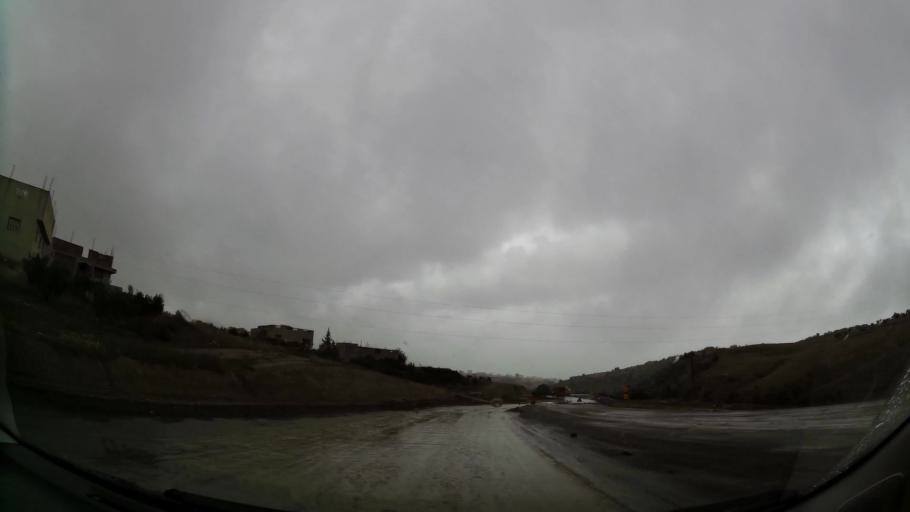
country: MA
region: Oriental
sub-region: Nador
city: Midar
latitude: 34.8890
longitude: -3.7515
